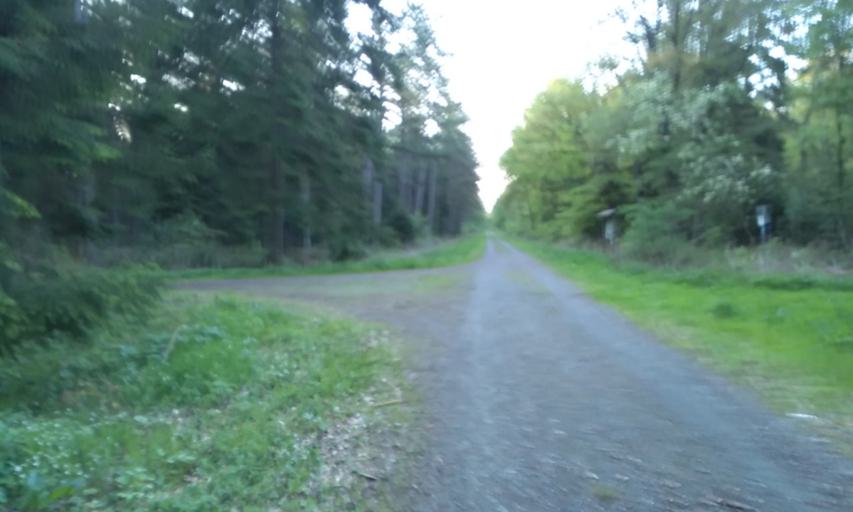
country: DE
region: Lower Saxony
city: Harsefeld
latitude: 53.4207
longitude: 9.4990
